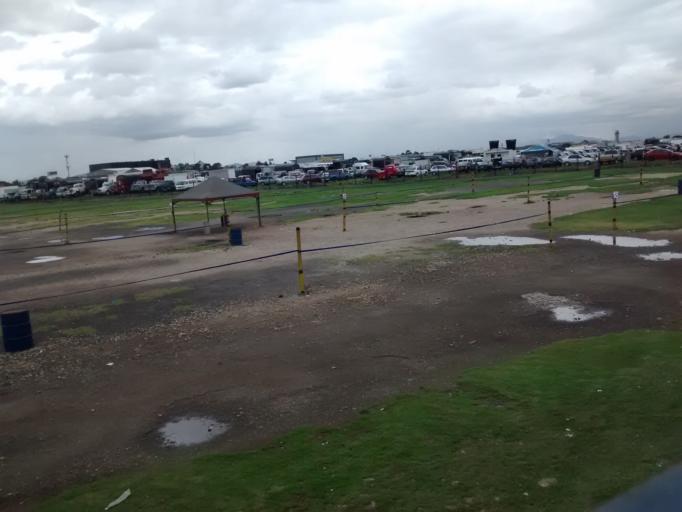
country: CO
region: Bogota D.C.
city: Bogota
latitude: 4.6895
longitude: -74.1191
